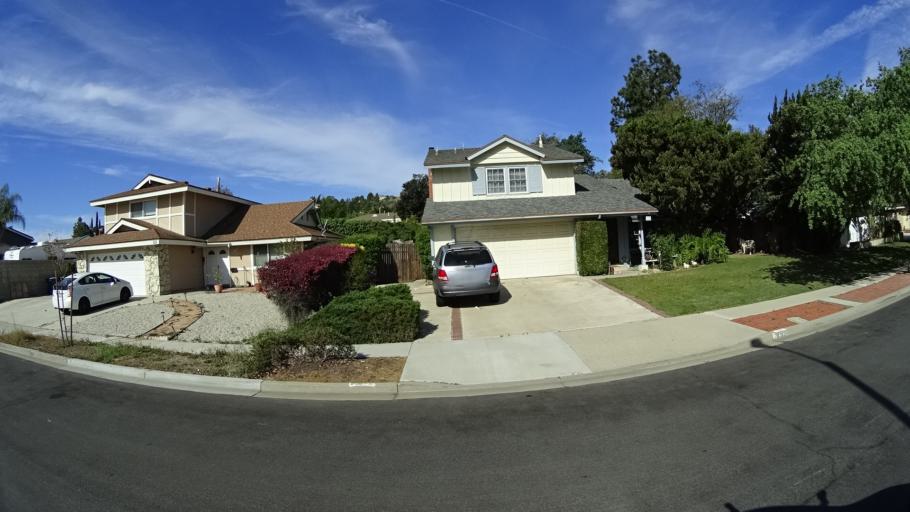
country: US
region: California
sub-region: Ventura County
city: Casa Conejo
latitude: 34.1770
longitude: -118.9557
